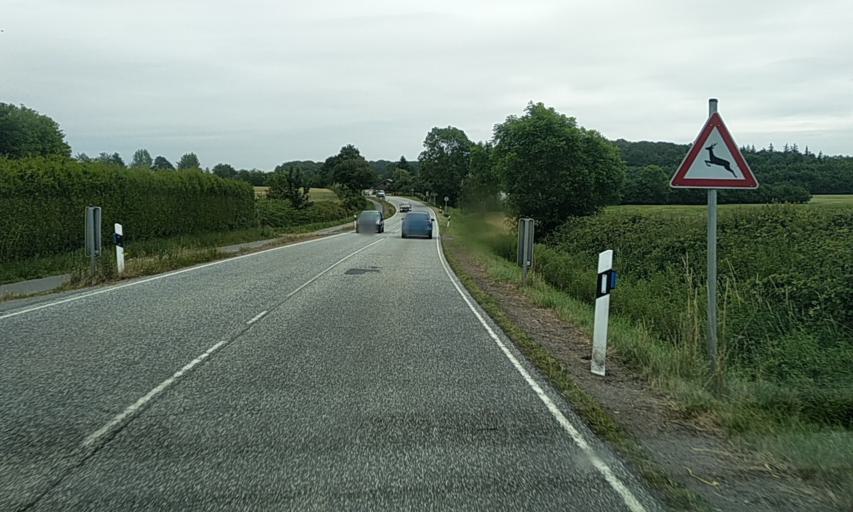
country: DE
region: Schleswig-Holstein
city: Rabenkirchen-Fauluck
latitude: 54.6465
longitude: 9.8798
